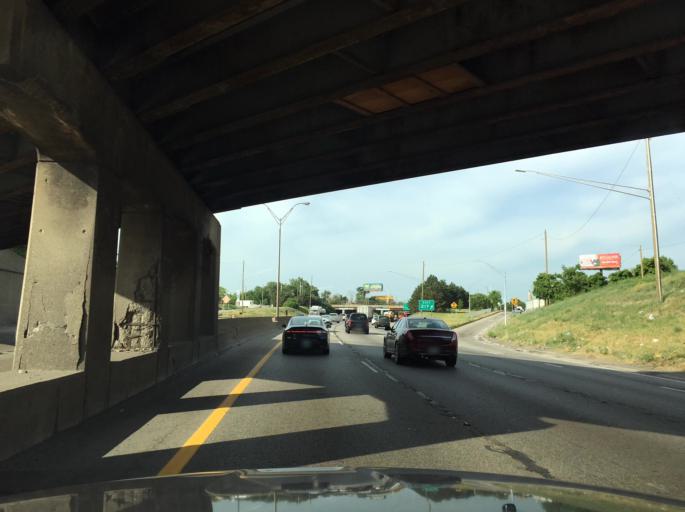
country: US
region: Michigan
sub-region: Wayne County
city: Hamtramck
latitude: 42.3811
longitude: -83.0319
